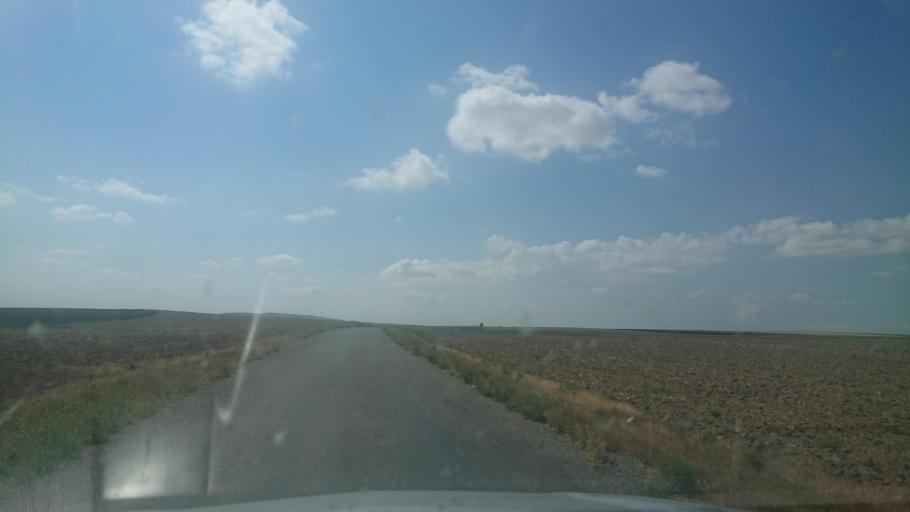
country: TR
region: Aksaray
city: Agacoren
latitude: 38.9971
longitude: 33.9800
